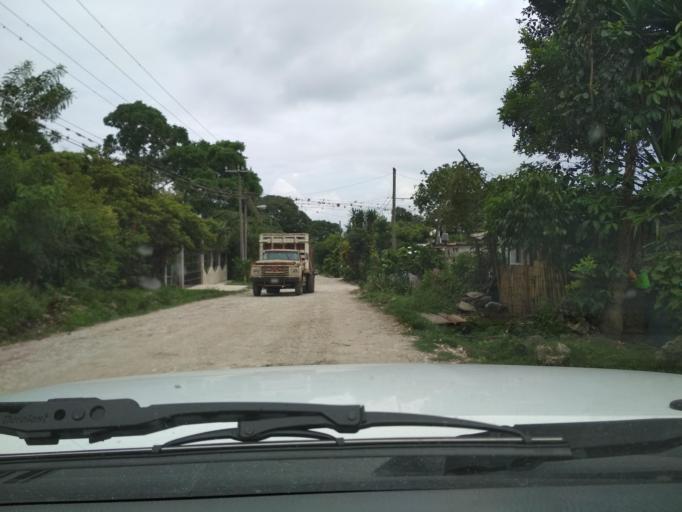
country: MX
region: Veracruz
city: Paraje Nuevo
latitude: 18.8782
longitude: -96.8793
